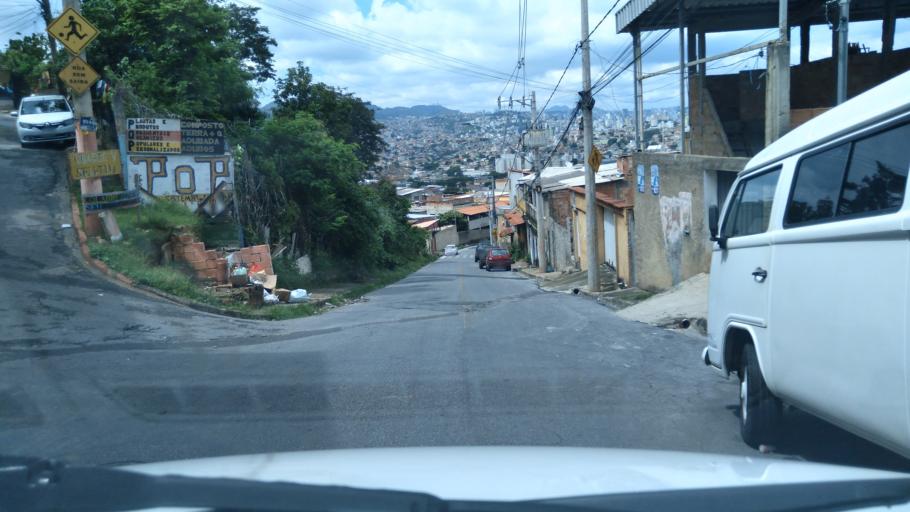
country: BR
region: Minas Gerais
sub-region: Belo Horizonte
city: Belo Horizonte
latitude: -19.8962
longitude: -43.8926
